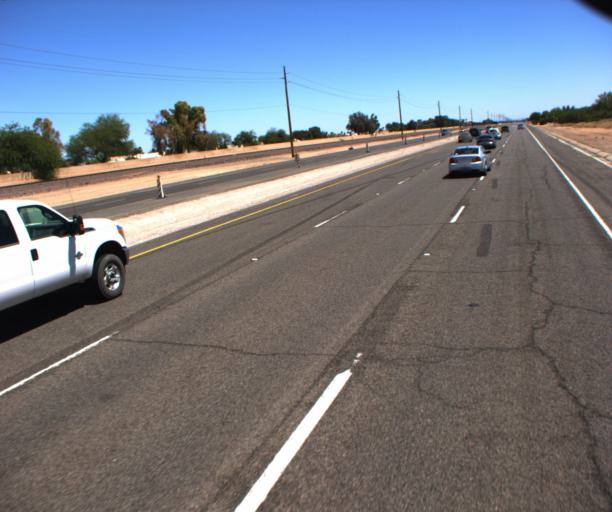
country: US
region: Arizona
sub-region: Maricopa County
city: Sun City West
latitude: 33.6769
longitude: -112.3994
